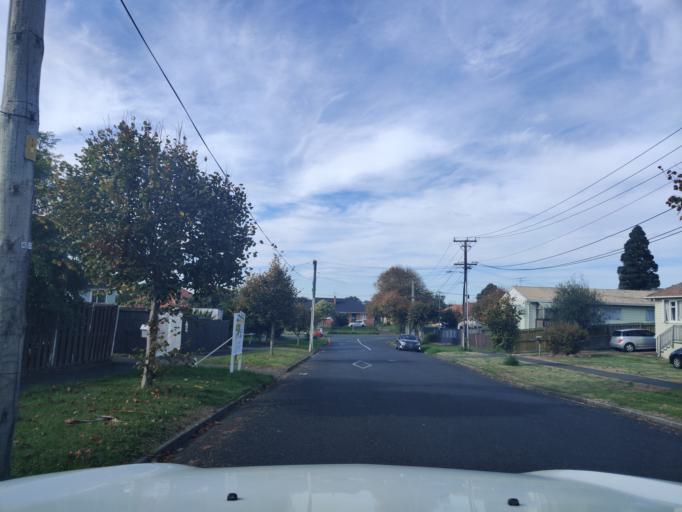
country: NZ
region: Auckland
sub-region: Auckland
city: Tamaki
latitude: -36.8976
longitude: 174.8591
